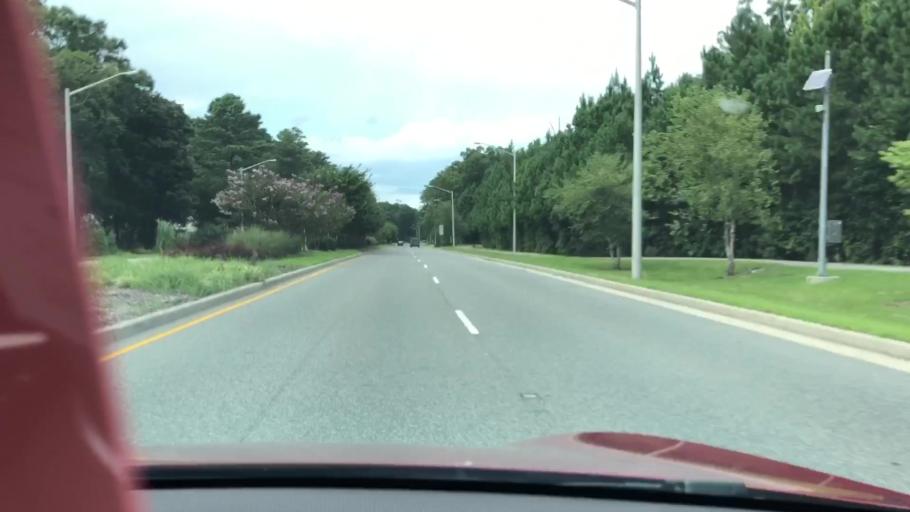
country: US
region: Virginia
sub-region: City of Virginia Beach
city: Virginia Beach
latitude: 36.8125
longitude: -75.9948
